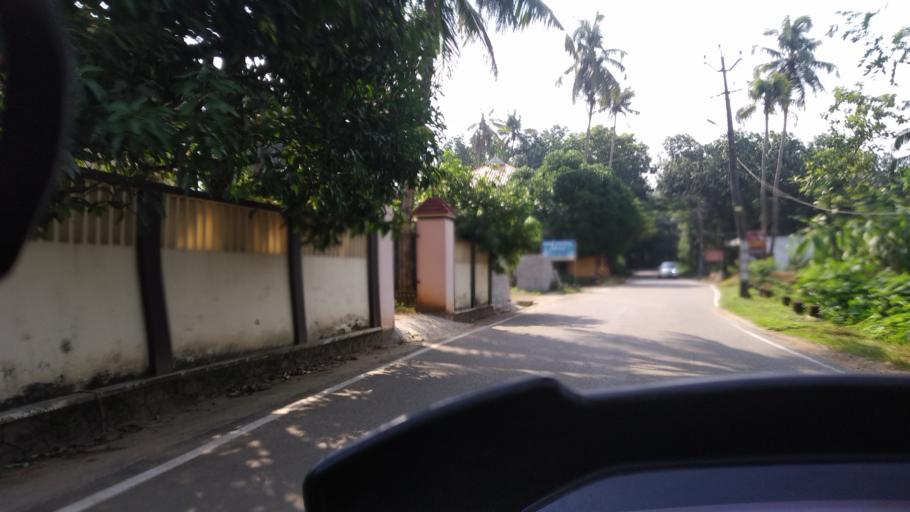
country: IN
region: Kerala
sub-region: Ernakulam
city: Piravam
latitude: 9.8574
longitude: 76.5207
